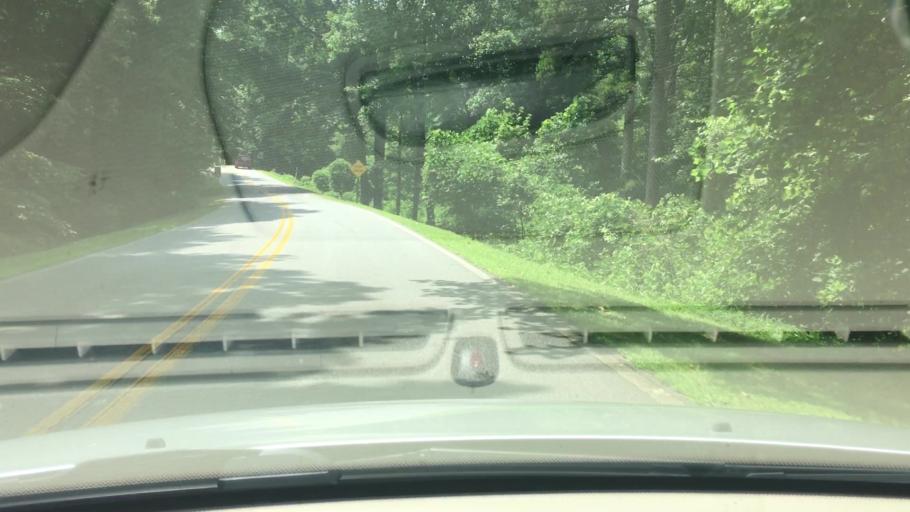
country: US
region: Georgia
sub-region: Dawson County
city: Dawsonville
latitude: 34.5564
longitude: -84.2507
